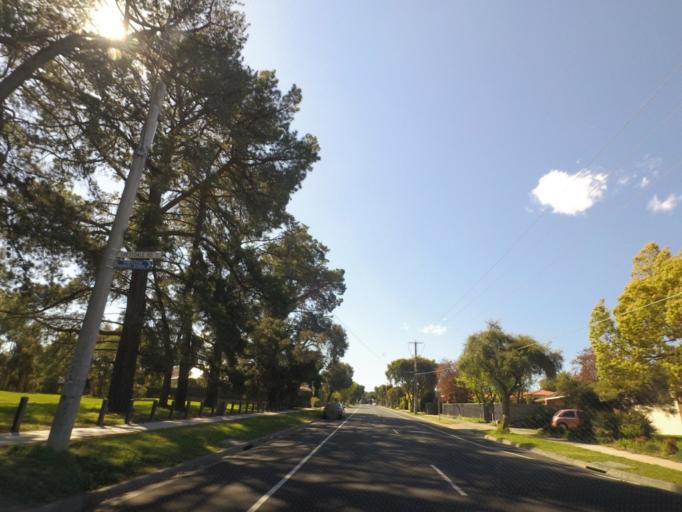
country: AU
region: Victoria
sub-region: Knox
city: Wantirna
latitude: -37.8599
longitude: 145.2273
